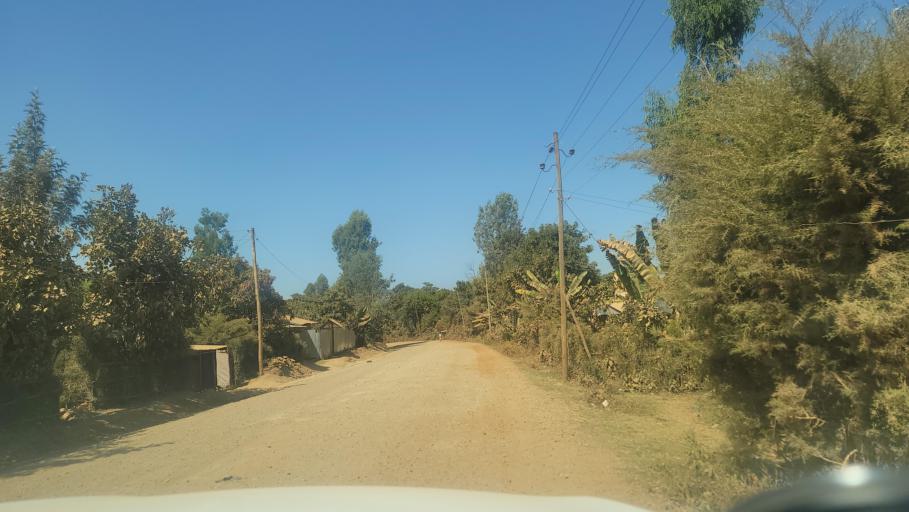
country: ET
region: Oromiya
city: Agaro
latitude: 7.8323
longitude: 36.5433
